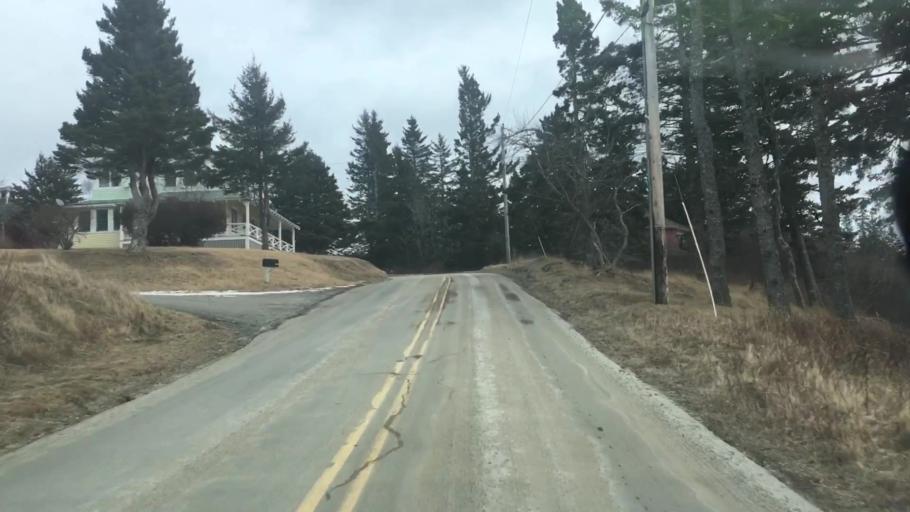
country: US
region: Maine
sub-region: Washington County
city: Machias
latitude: 44.6116
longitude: -67.4817
